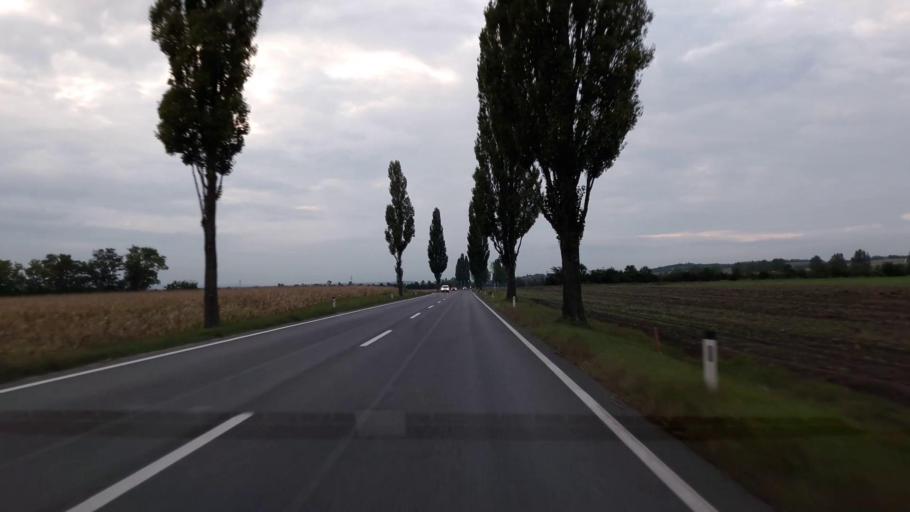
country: AT
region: Lower Austria
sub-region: Politischer Bezirk Bruck an der Leitha
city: Trautmannsdorf an der Leitha
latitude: 48.0421
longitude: 16.6666
